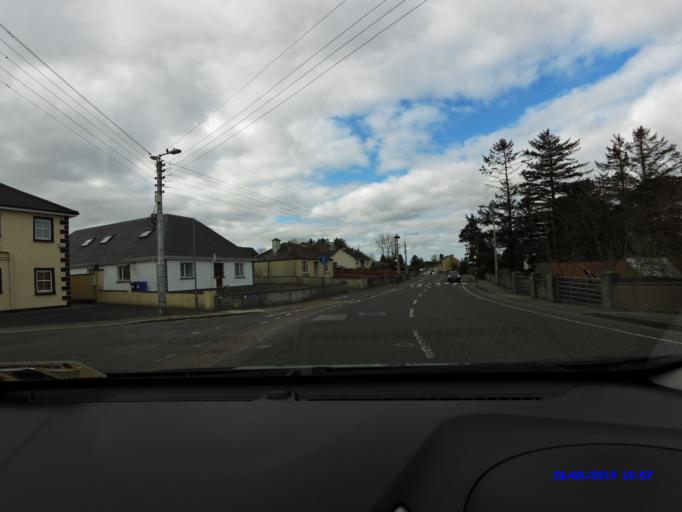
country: IE
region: Connaught
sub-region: Maigh Eo
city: Castlebar
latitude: 53.8567
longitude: -9.3158
